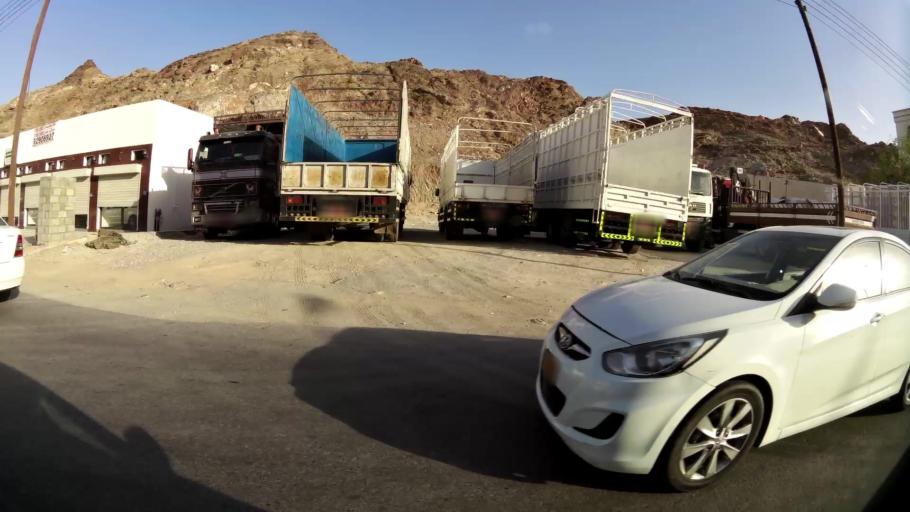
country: OM
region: Muhafazat Masqat
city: Muscat
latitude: 23.5844
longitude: 58.5472
